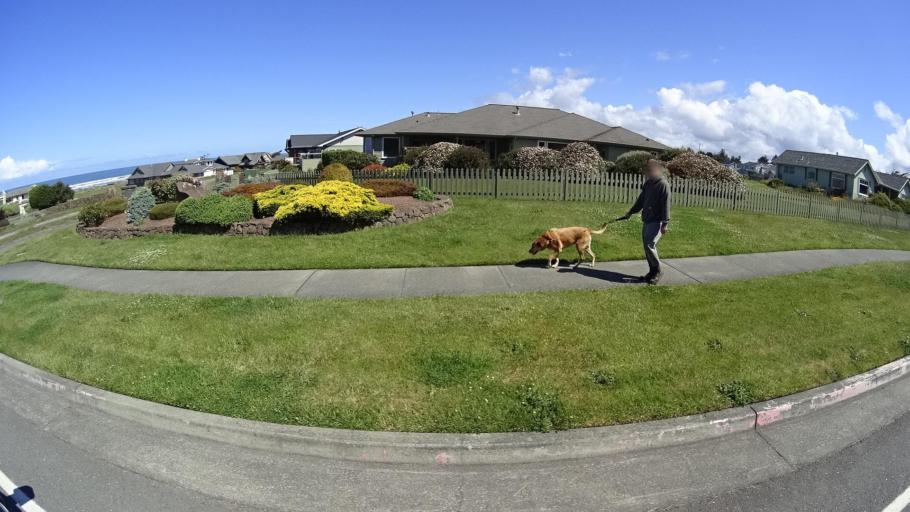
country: US
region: California
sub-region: Humboldt County
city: McKinleyville
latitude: 40.9561
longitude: -124.1210
